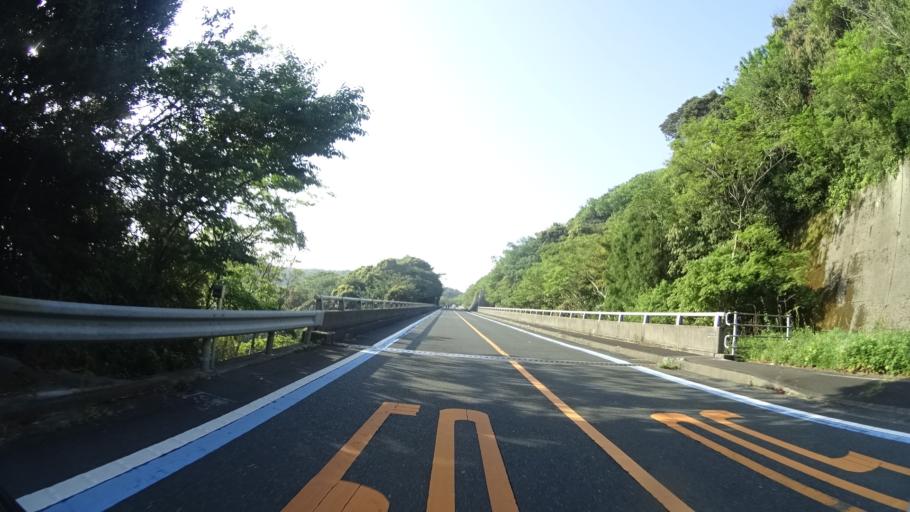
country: JP
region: Ehime
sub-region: Nishiuwa-gun
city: Ikata-cho
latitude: 33.4626
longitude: 132.2718
